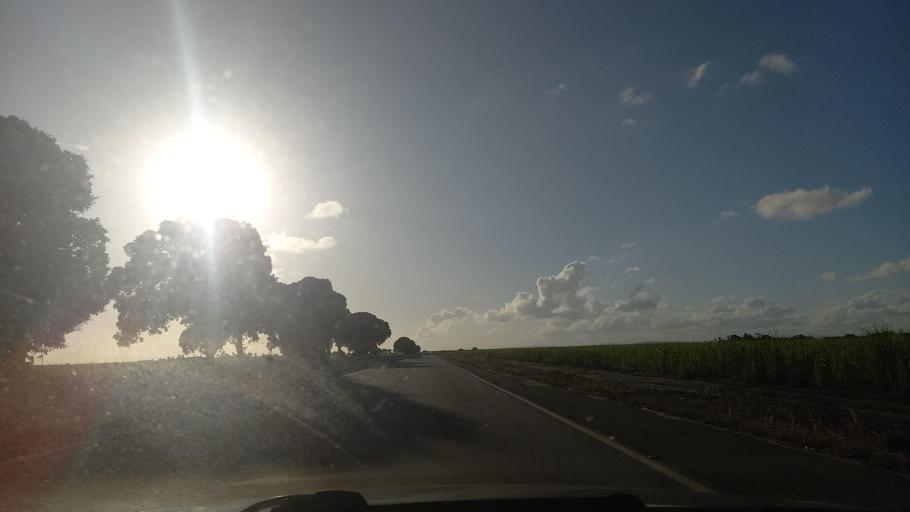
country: BR
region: Alagoas
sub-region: Campo Alegre
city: Campo Alegre
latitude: -9.8116
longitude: -36.2561
